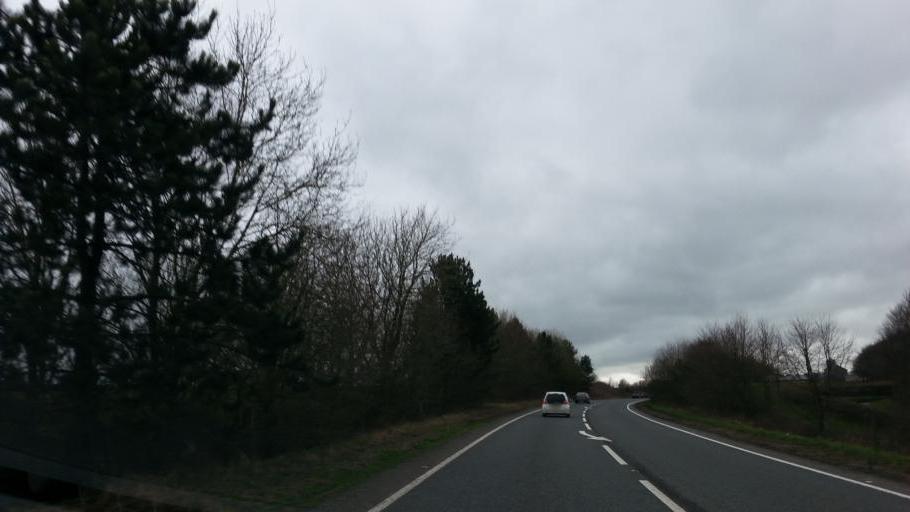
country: GB
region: England
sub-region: Devon
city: Tiverton
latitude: 50.9595
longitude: -3.6191
